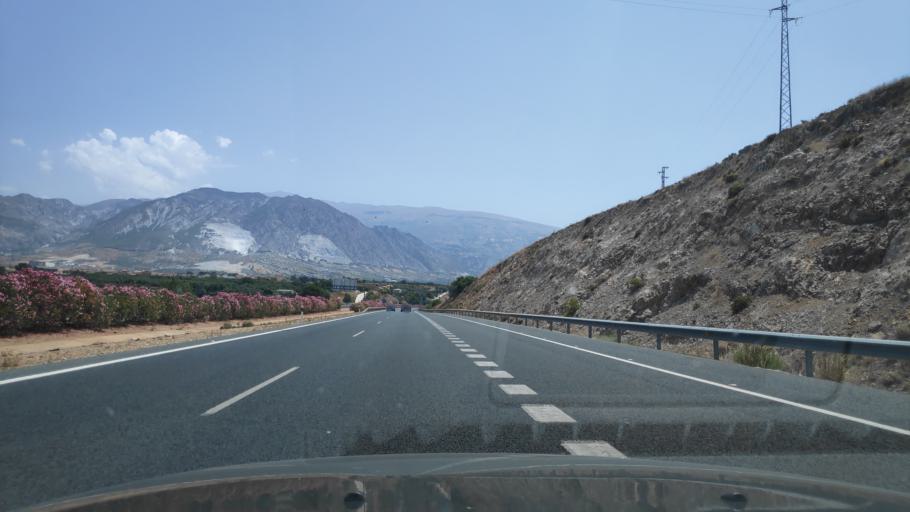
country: ES
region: Andalusia
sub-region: Provincia de Granada
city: Durcal
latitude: 36.9877
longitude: -3.6016
